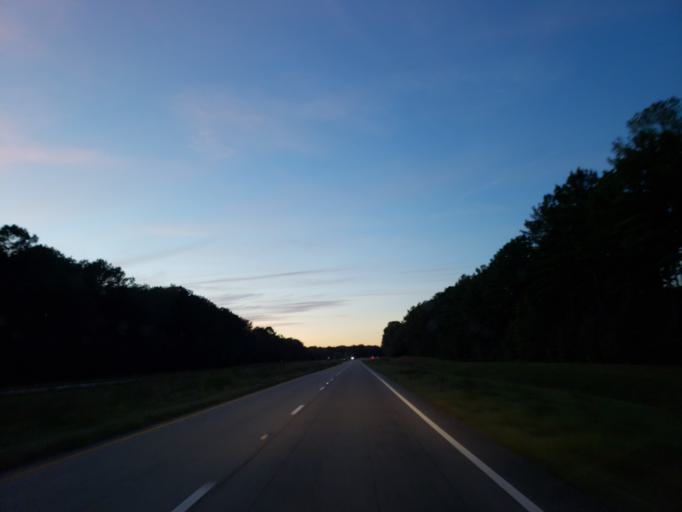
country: US
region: Mississippi
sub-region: Wayne County
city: Waynesboro
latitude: 31.8447
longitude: -88.7114
